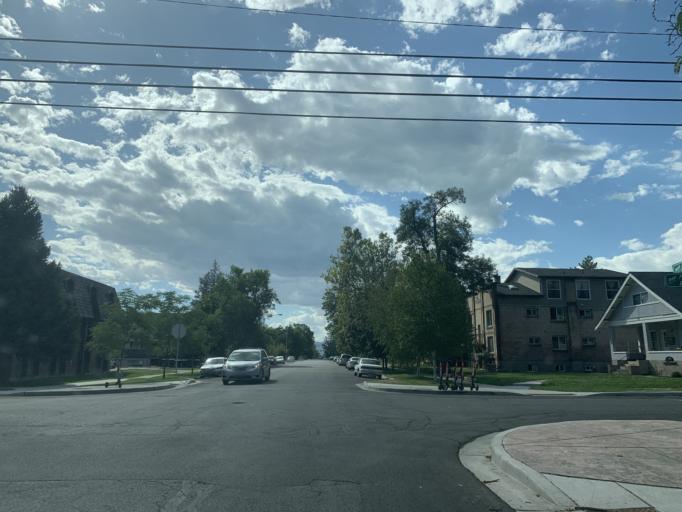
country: US
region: Utah
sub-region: Utah County
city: Provo
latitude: 40.2391
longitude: -111.6550
